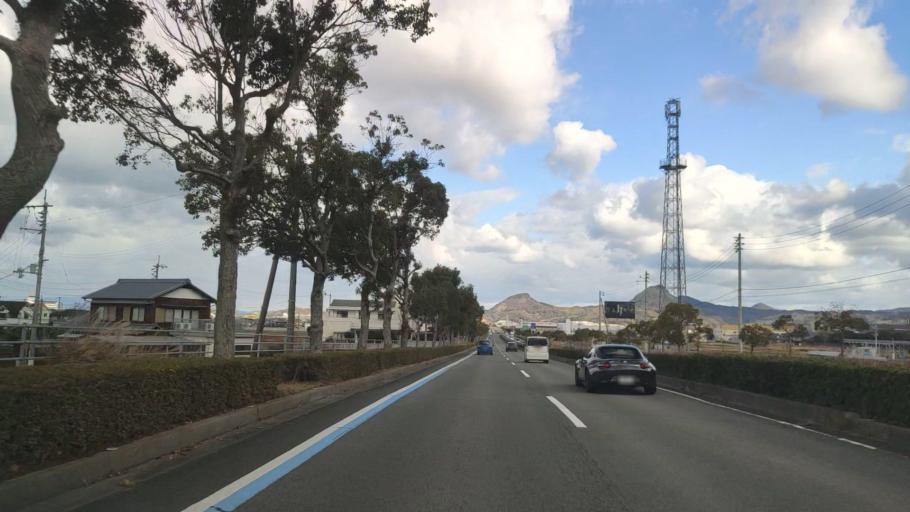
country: JP
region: Ehime
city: Hojo
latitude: 33.9550
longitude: 132.7757
